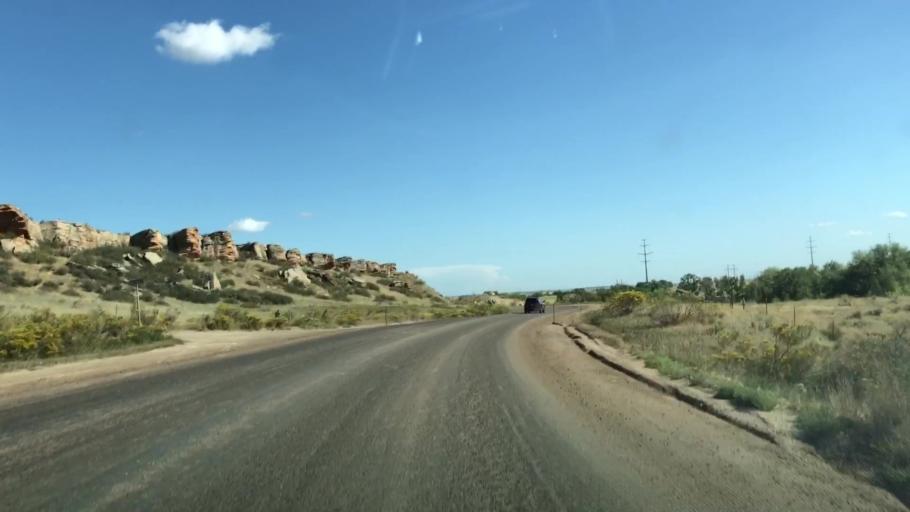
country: US
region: Colorado
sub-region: Larimer County
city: Laporte
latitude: 40.7764
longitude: -105.1417
